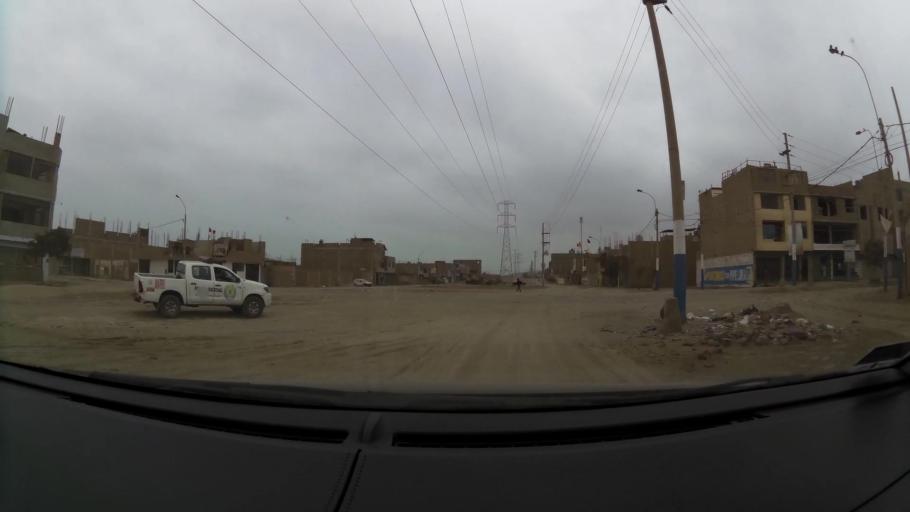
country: PE
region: Lima
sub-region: Lima
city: Independencia
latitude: -11.9613
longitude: -77.0991
